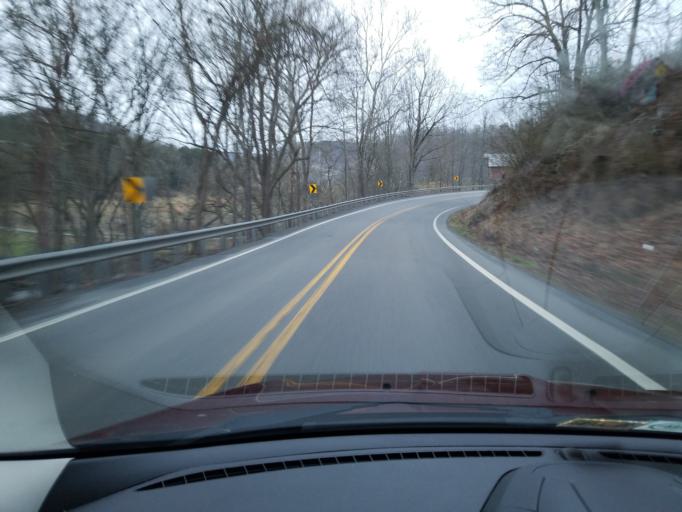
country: US
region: West Virginia
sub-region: Monroe County
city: Union
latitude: 37.5595
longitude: -80.5690
